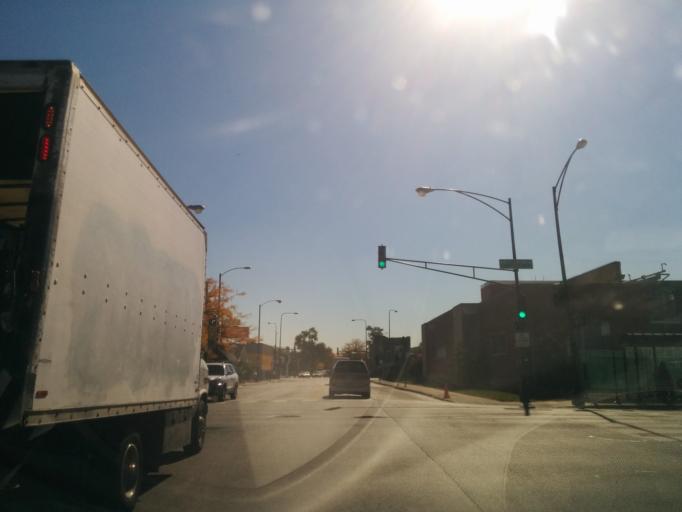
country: US
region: Illinois
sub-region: Cook County
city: Elmwood Park
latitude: 41.9238
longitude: -87.7855
